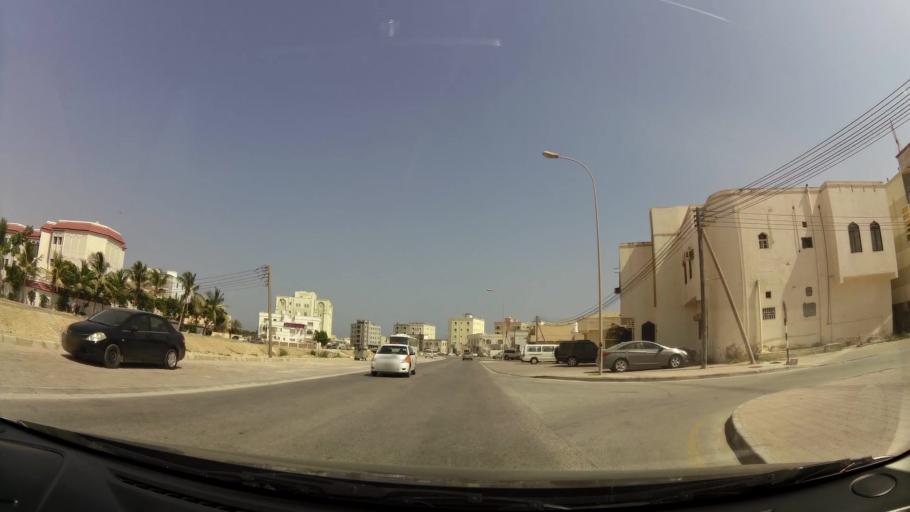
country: OM
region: Zufar
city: Salalah
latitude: 17.0163
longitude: 54.0596
